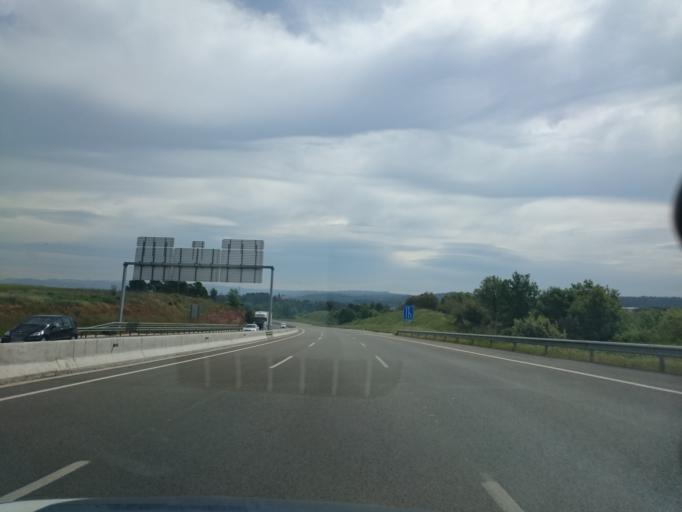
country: ES
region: Catalonia
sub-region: Provincia de Barcelona
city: Navarcles
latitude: 41.7797
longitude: 1.8975
